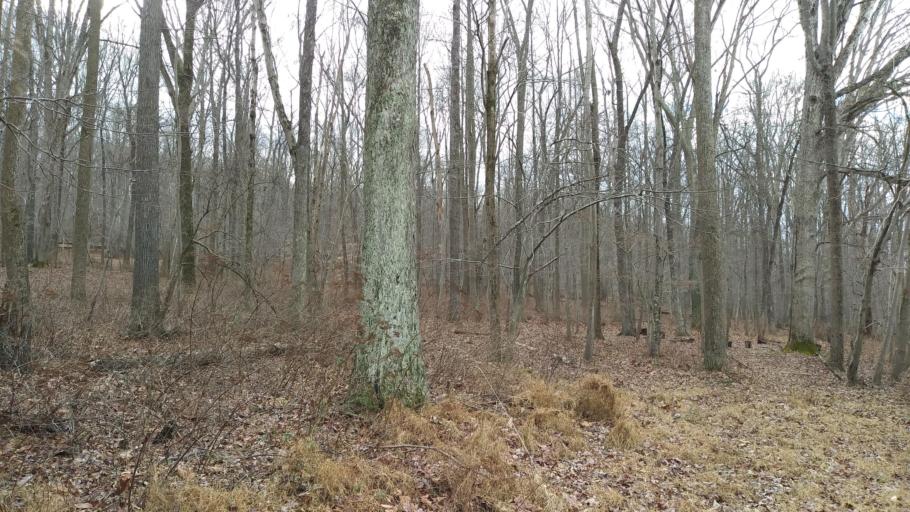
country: US
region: Pennsylvania
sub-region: York County
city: Susquehanna Trails
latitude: 39.6853
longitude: -76.2709
